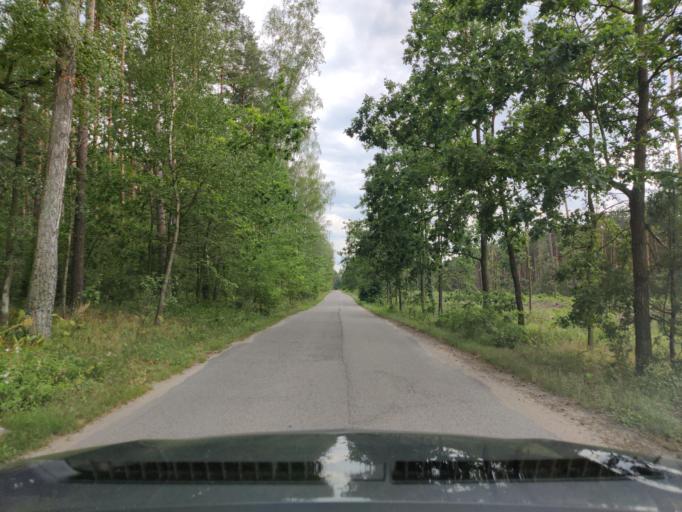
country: PL
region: Masovian Voivodeship
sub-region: Powiat pultuski
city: Pultusk
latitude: 52.7344
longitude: 21.1371
